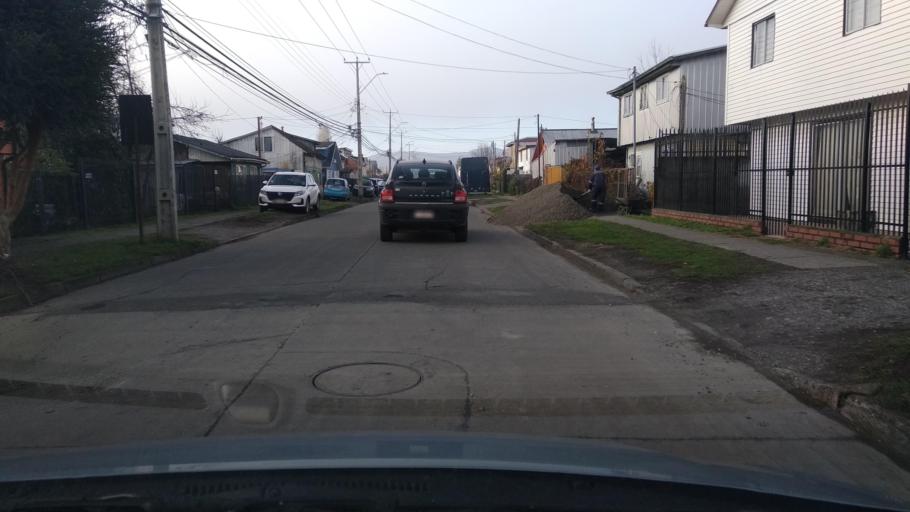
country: CL
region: Los Lagos
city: Las Animas
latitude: -39.8103
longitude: -73.2268
